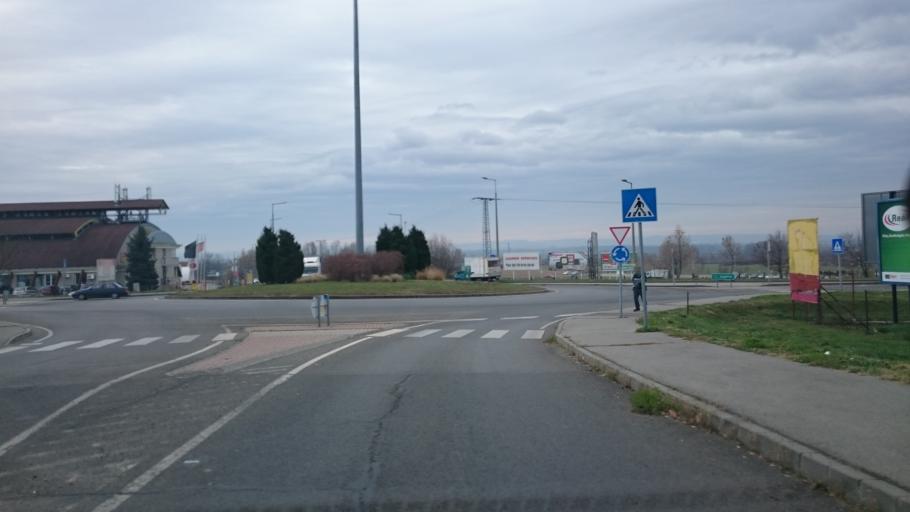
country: HU
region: Baranya
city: Pellerd
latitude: 46.0655
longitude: 18.1729
